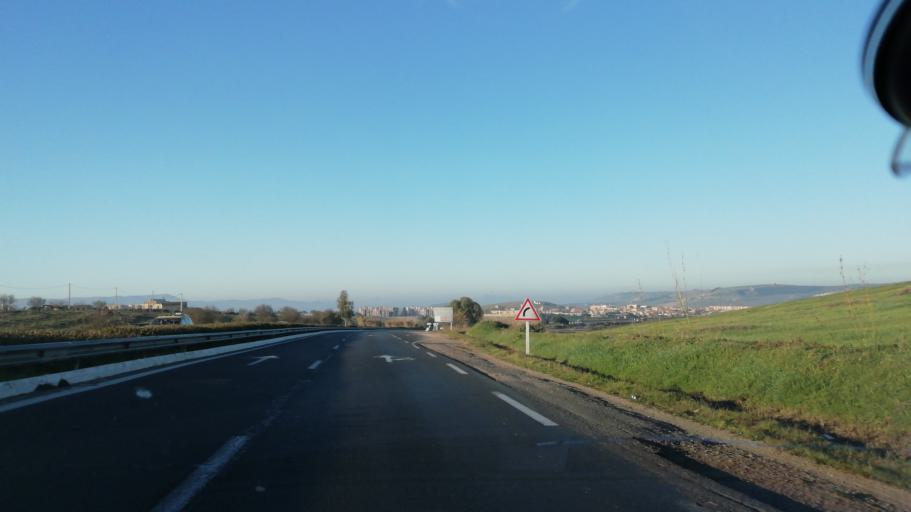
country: DZ
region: Ain Temouchent
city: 'Ain Temouchent
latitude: 35.2626
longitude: -1.2465
